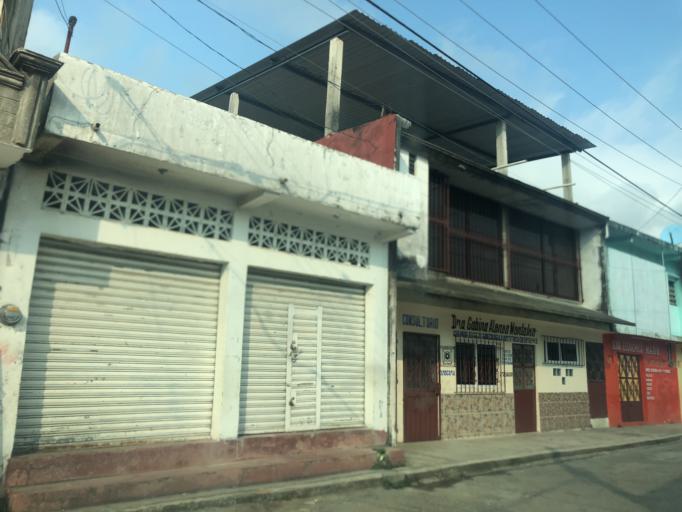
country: MX
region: Chiapas
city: Pichucalco
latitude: 17.5117
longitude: -93.1154
